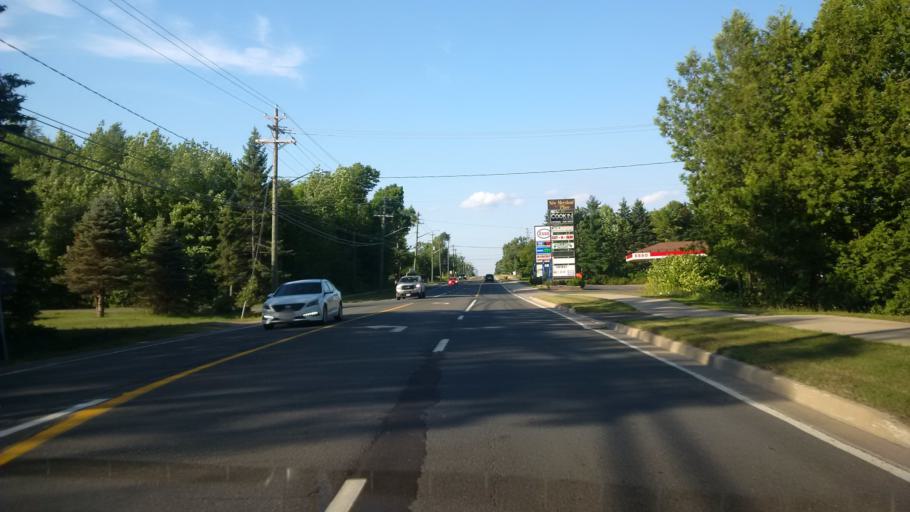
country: CA
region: New Brunswick
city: Fredericton
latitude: 45.8876
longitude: -66.6869
